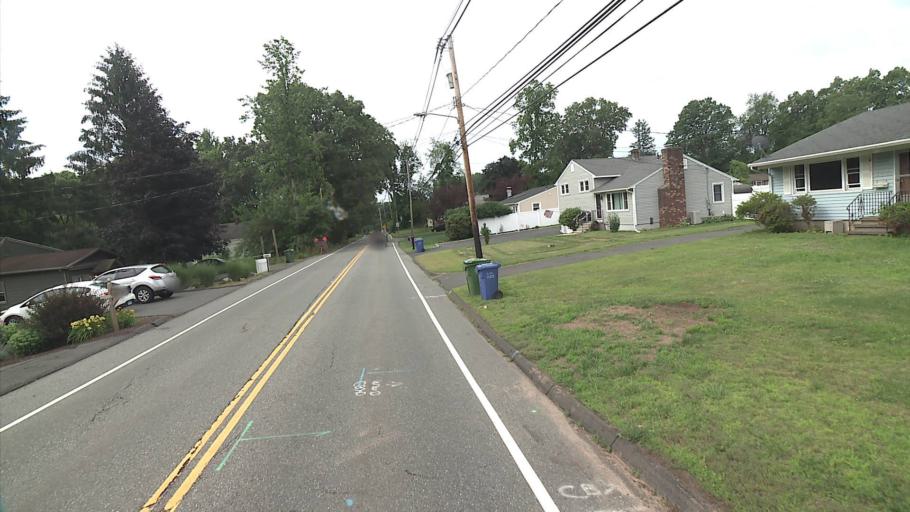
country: US
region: Connecticut
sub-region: New Haven County
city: Wallingford Center
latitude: 41.4400
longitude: -72.8048
